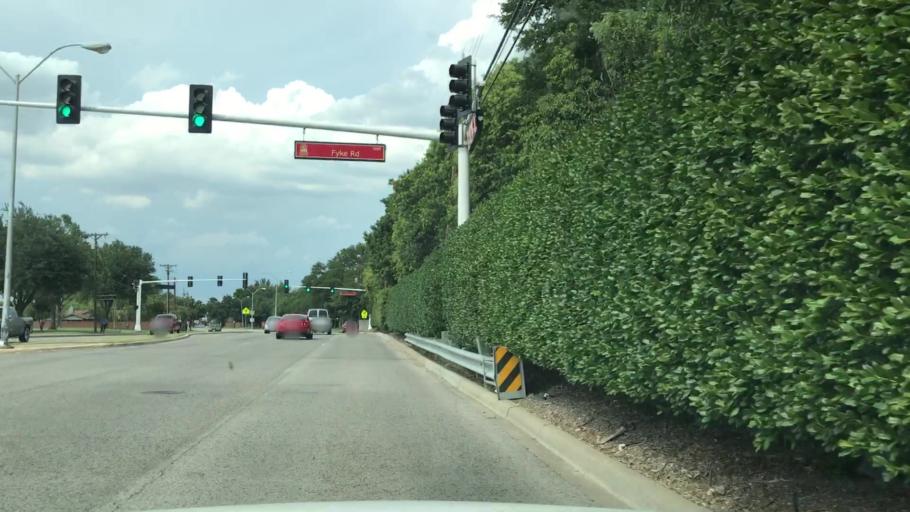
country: US
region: Texas
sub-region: Dallas County
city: Carrollton
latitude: 32.9462
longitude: -96.8718
